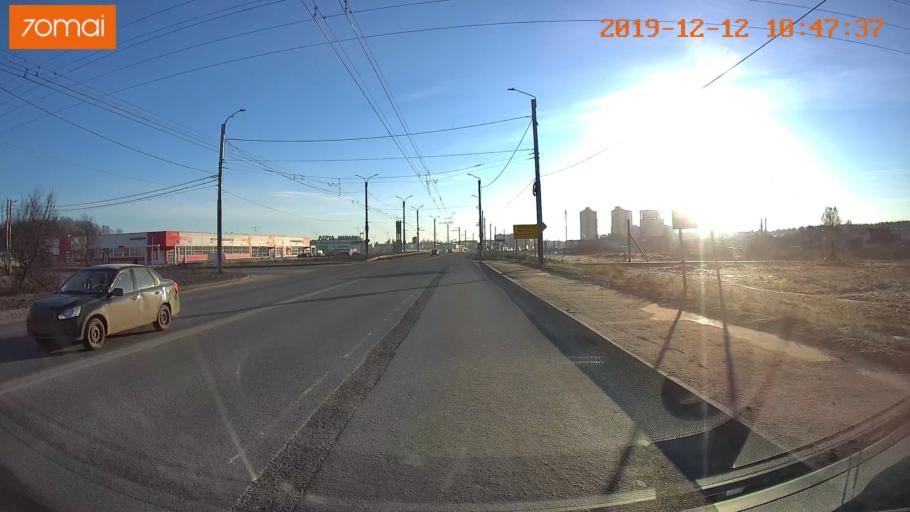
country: RU
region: Ivanovo
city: Kokhma
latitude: 56.9485
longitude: 41.0521
